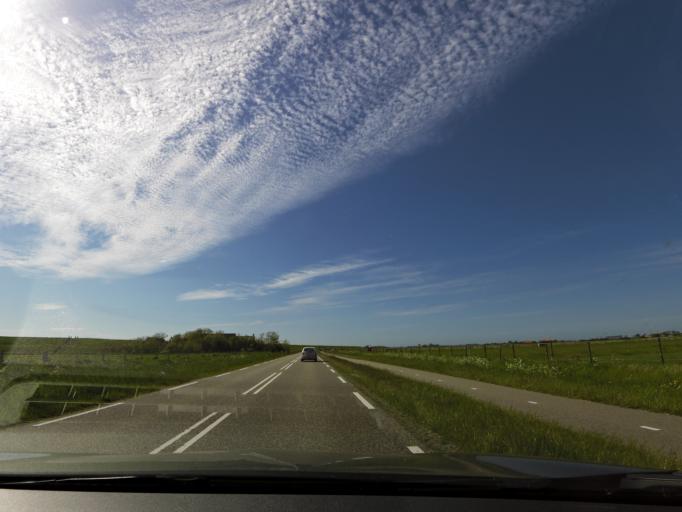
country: NL
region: Zeeland
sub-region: Schouwen-Duiveland
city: Scharendijke
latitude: 51.6672
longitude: 3.8808
